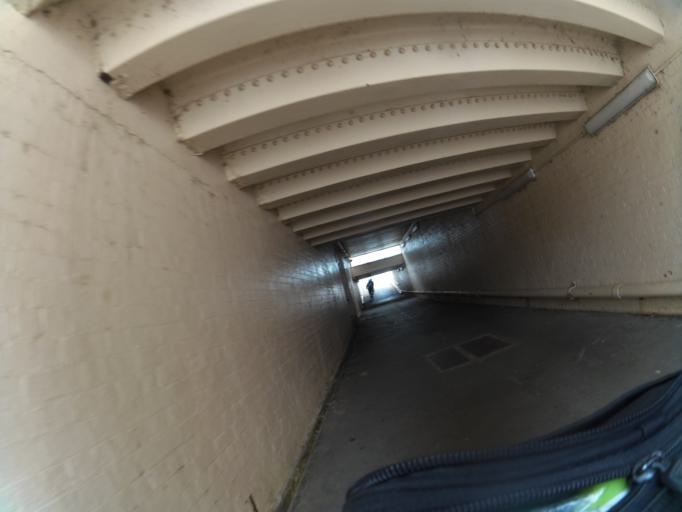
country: AU
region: Victoria
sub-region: Mount Alexander
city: Castlemaine
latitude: -37.0633
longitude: 144.2134
